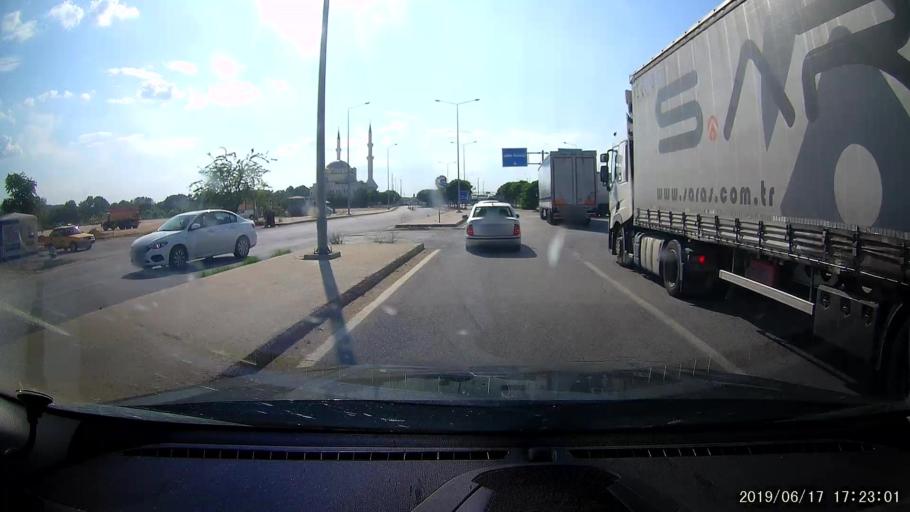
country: GR
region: East Macedonia and Thrace
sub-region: Nomos Evrou
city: Rizia
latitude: 41.7134
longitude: 26.3683
